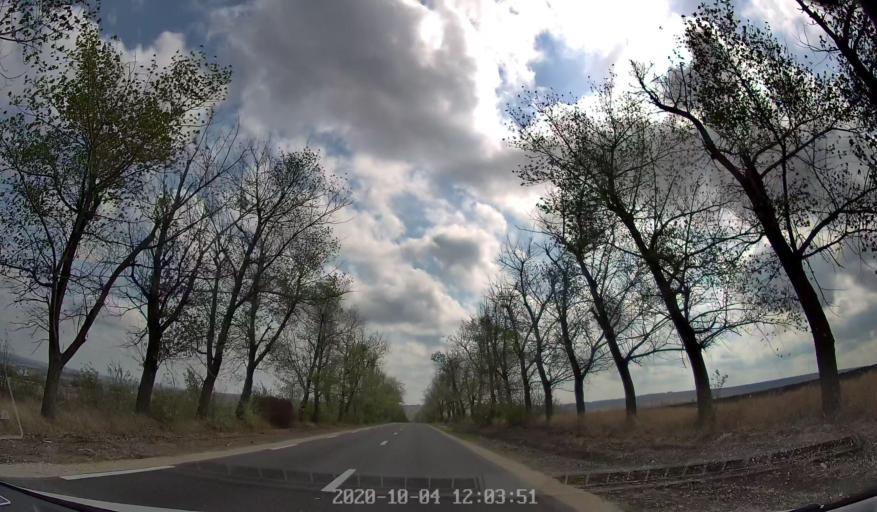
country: MD
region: Rezina
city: Saharna
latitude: 47.6089
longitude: 28.9342
